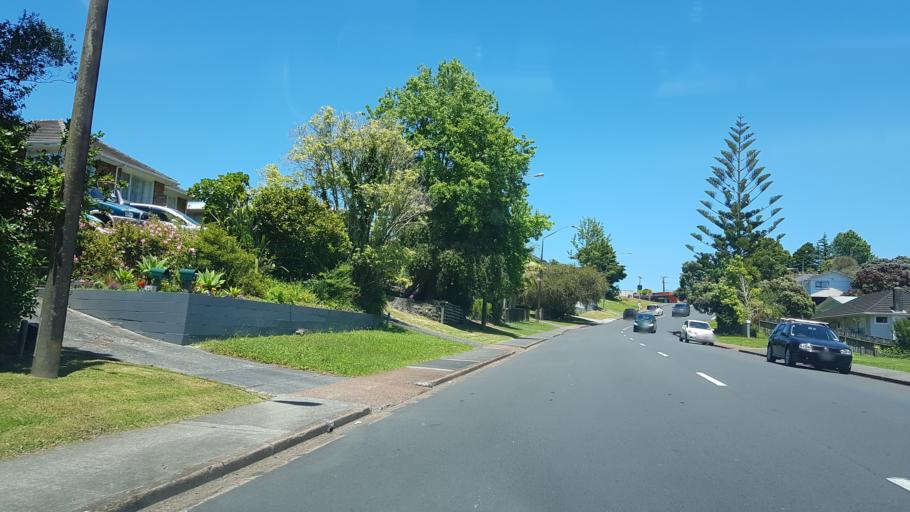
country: NZ
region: Auckland
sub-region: Auckland
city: North Shore
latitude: -36.7782
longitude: 174.7308
